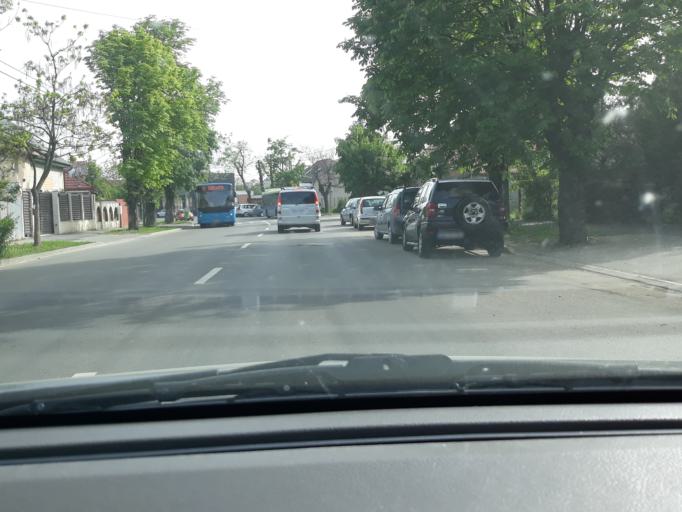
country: RO
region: Bihor
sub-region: Comuna Biharea
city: Oradea
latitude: 47.0409
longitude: 21.9553
